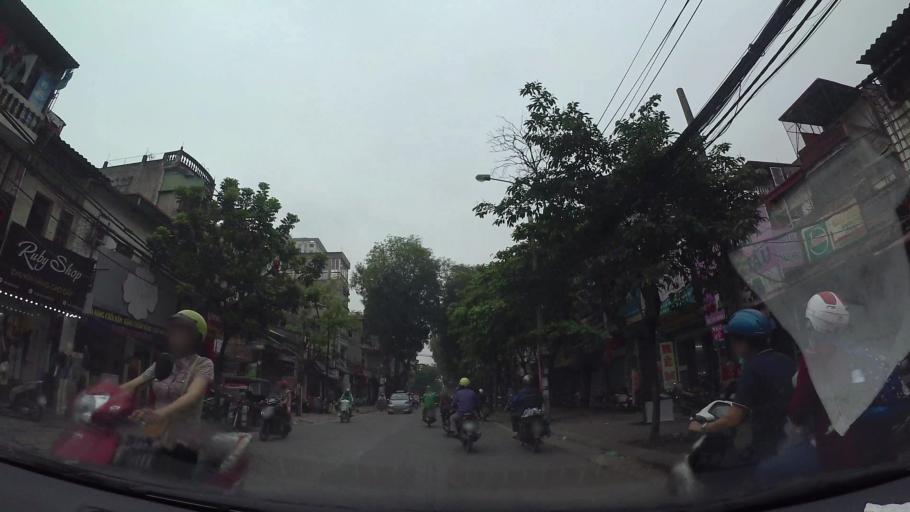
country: VN
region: Ha Noi
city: Hai BaTrung
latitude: 20.9954
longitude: 105.8545
